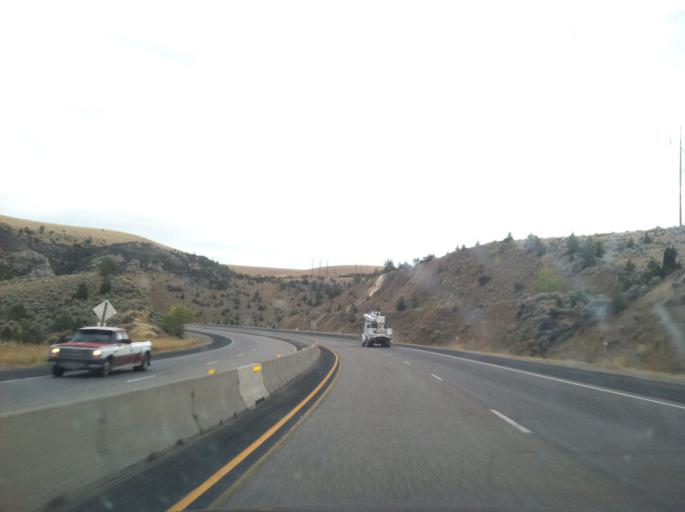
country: US
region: Montana
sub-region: Jefferson County
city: Whitehall
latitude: 45.8771
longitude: -111.8967
